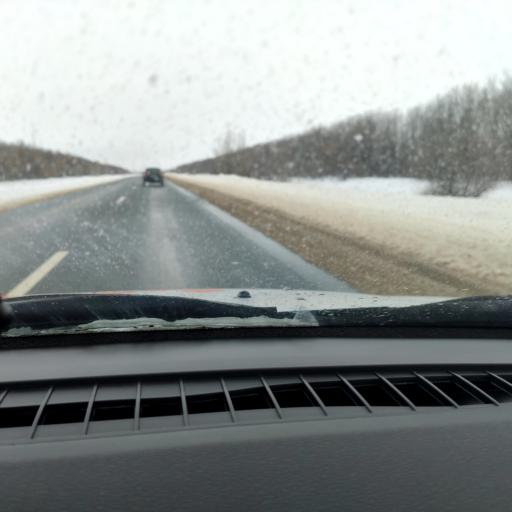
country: RU
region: Samara
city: Mayskoye
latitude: 52.4812
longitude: 50.5372
